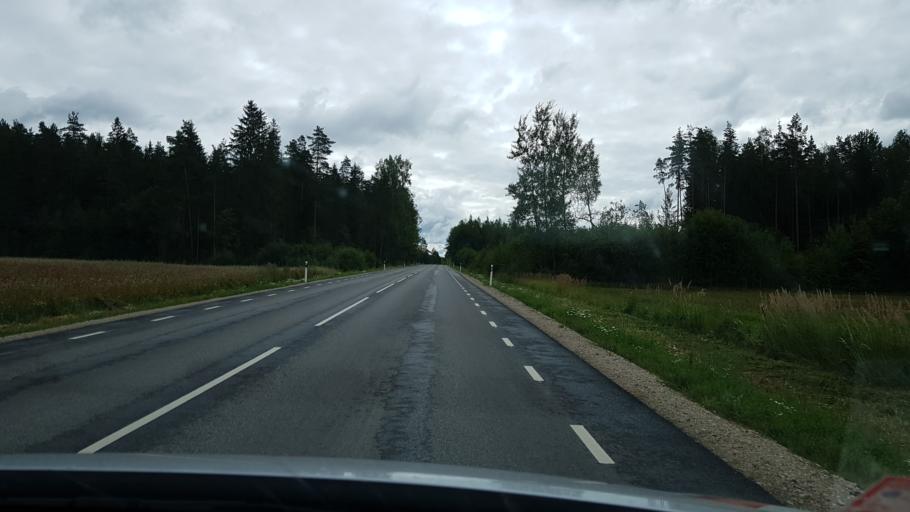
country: EE
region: Polvamaa
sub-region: Polva linn
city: Polva
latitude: 58.0101
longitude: 27.1867
